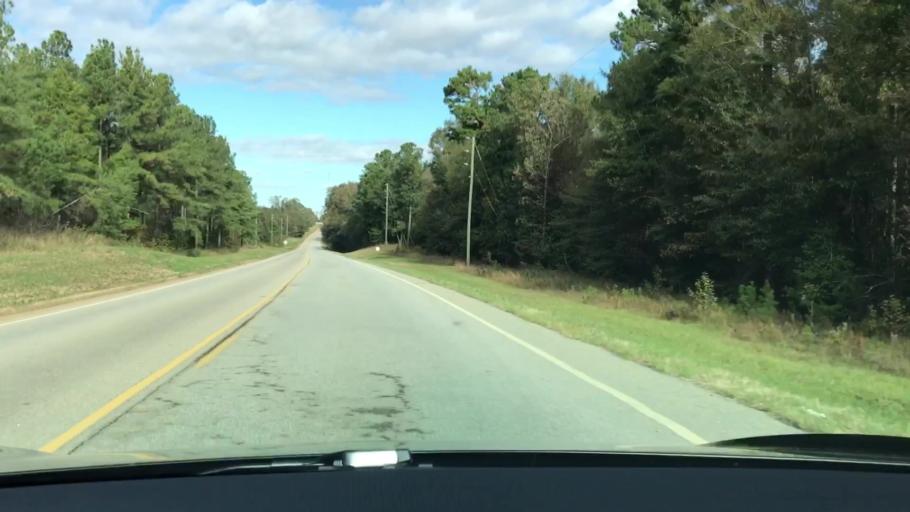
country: US
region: Georgia
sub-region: Jefferson County
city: Louisville
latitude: 33.0899
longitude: -82.4157
